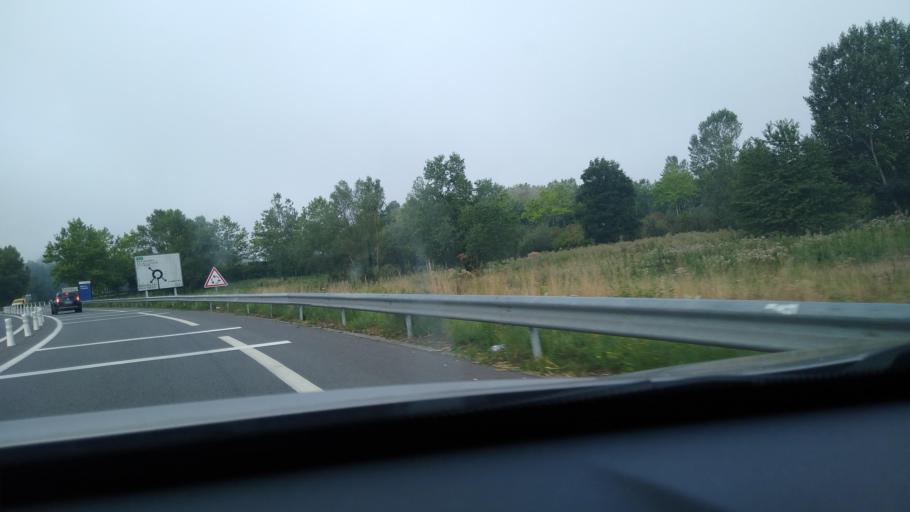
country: FR
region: Midi-Pyrenees
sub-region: Departement de la Haute-Garonne
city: Salies-du-Salat
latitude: 43.1245
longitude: 0.9373
